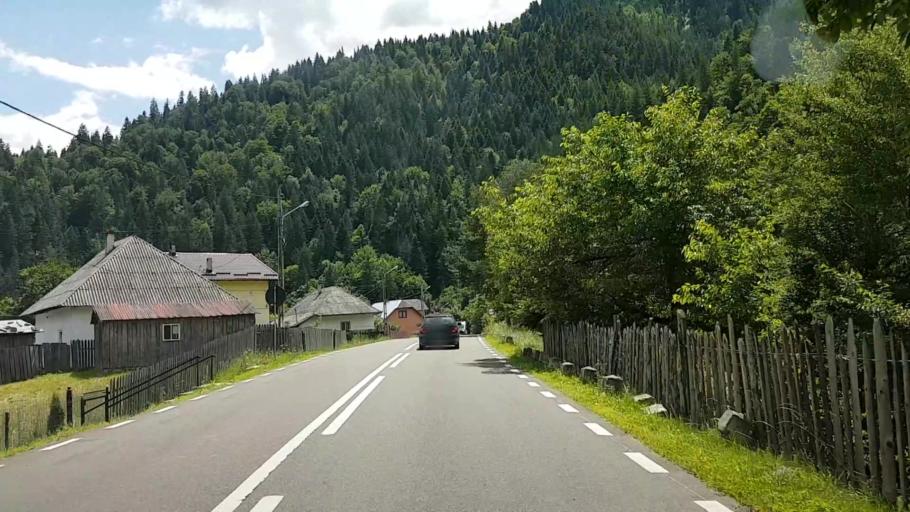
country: RO
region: Suceava
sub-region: Comuna Brosteni
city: Brosteni
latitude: 47.2583
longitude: 25.6696
